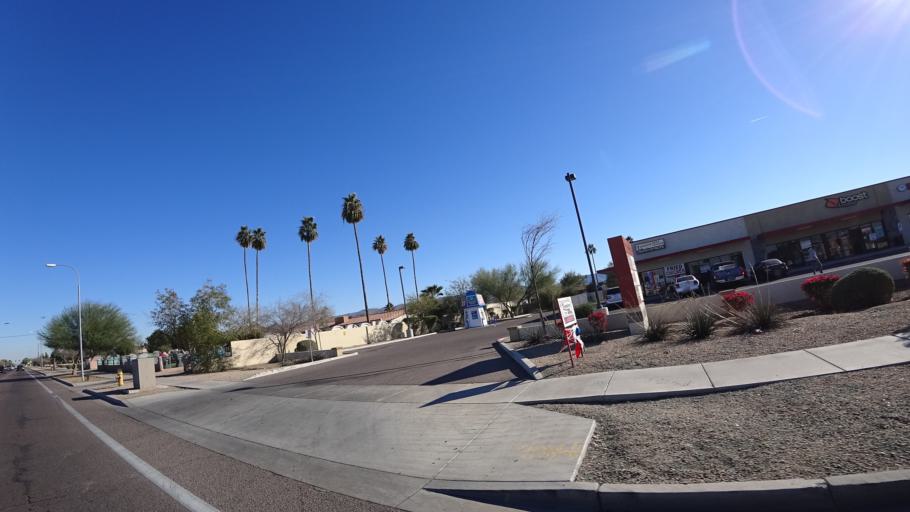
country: US
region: Arizona
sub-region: Maricopa County
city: Phoenix
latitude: 33.3922
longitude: -112.0959
